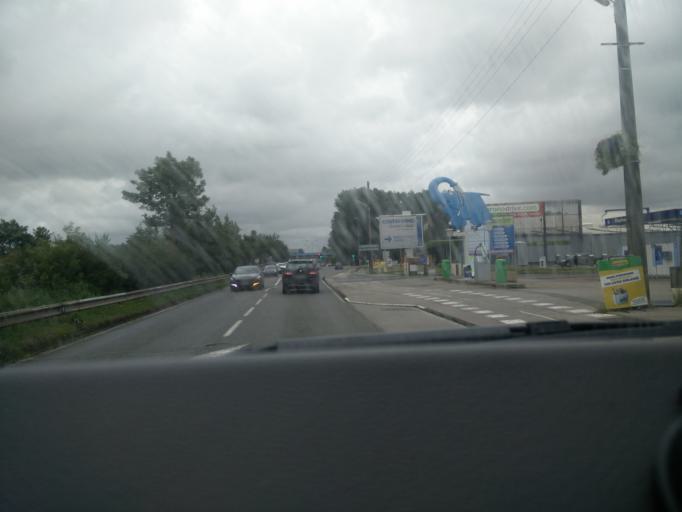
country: FR
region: Nord-Pas-de-Calais
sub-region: Departement du Nord
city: Dunkerque
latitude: 51.0161
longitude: 2.3778
